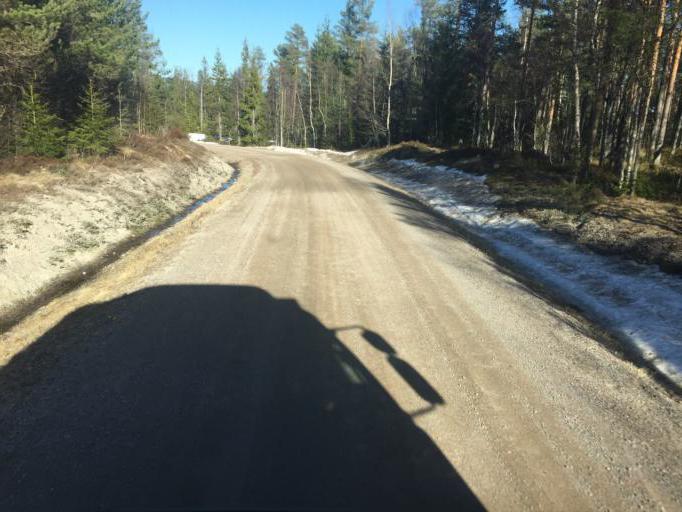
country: SE
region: Vaermland
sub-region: Filipstads Kommun
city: Lesjofors
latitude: 60.2487
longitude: 14.0910
